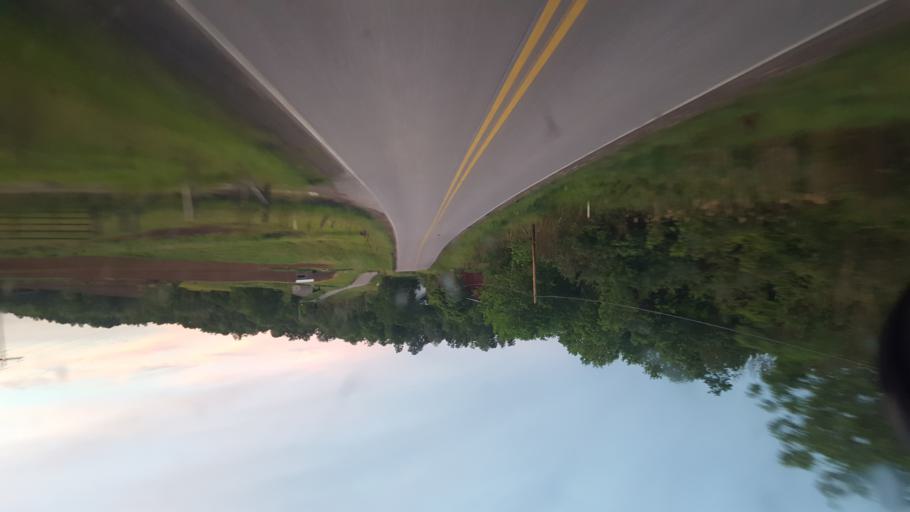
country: US
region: Ohio
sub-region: Belmont County
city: Barnesville
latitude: 40.0751
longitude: -81.3206
